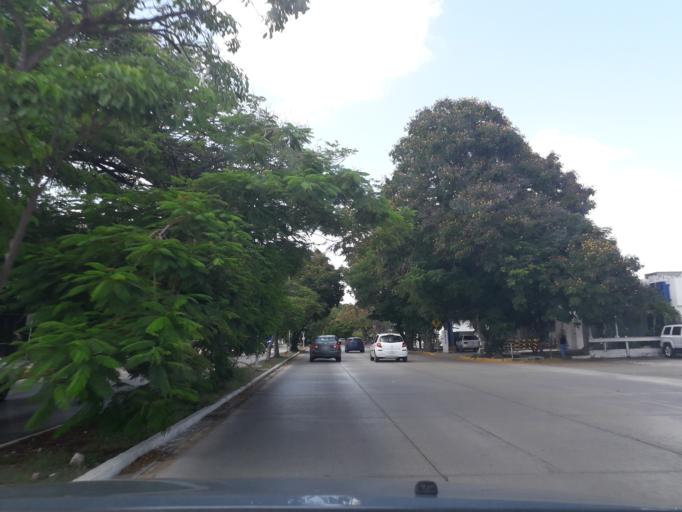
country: MX
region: Yucatan
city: Merida
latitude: 21.0042
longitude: -89.6150
